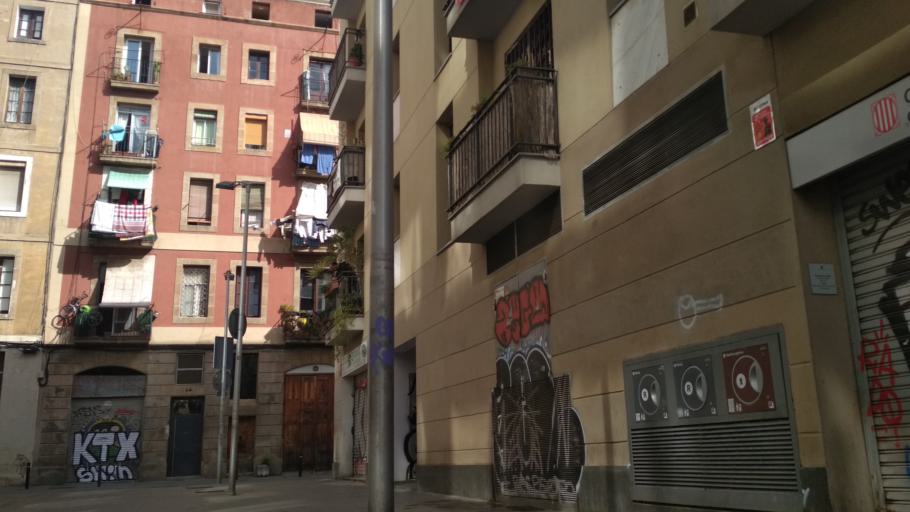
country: ES
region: Catalonia
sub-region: Provincia de Barcelona
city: Ciutat Vella
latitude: 41.3792
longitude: 2.1702
